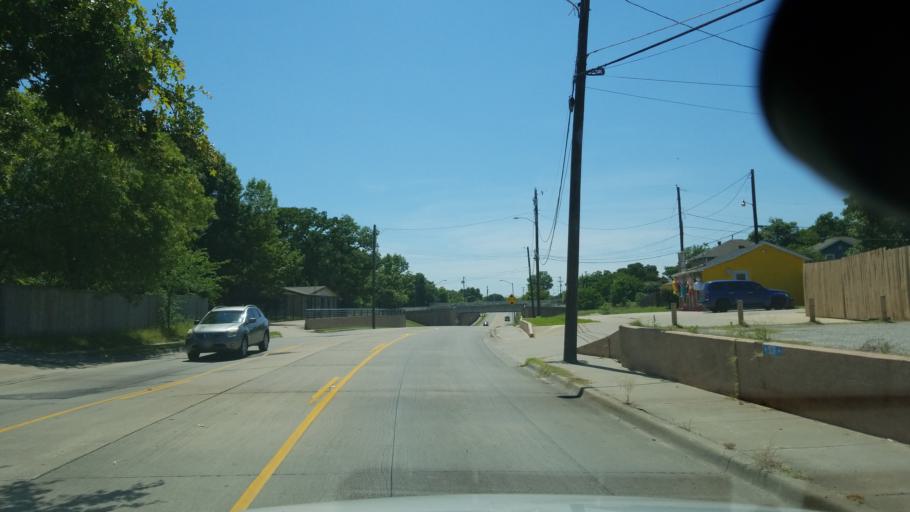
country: US
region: Texas
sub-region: Dallas County
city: Irving
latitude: 32.8295
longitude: -96.9394
